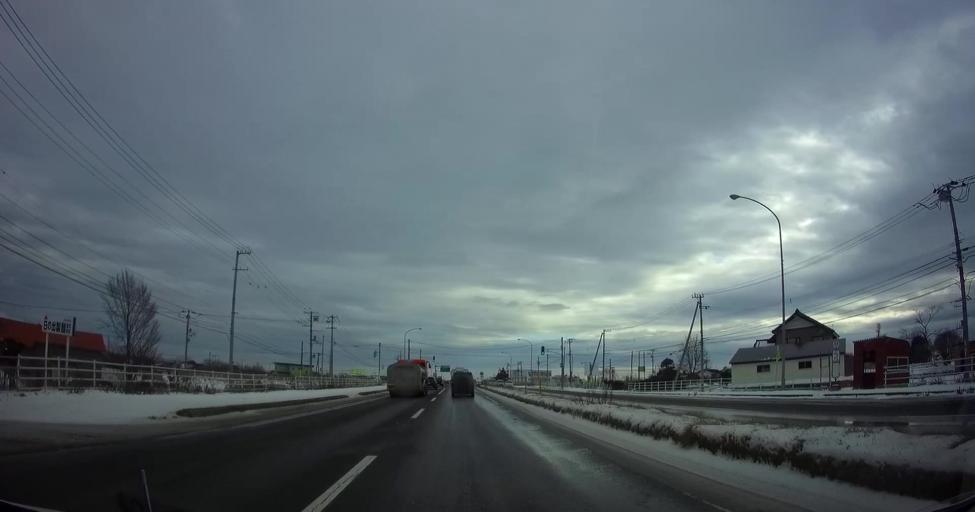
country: JP
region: Hokkaido
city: Nanae
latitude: 41.8395
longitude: 140.6894
